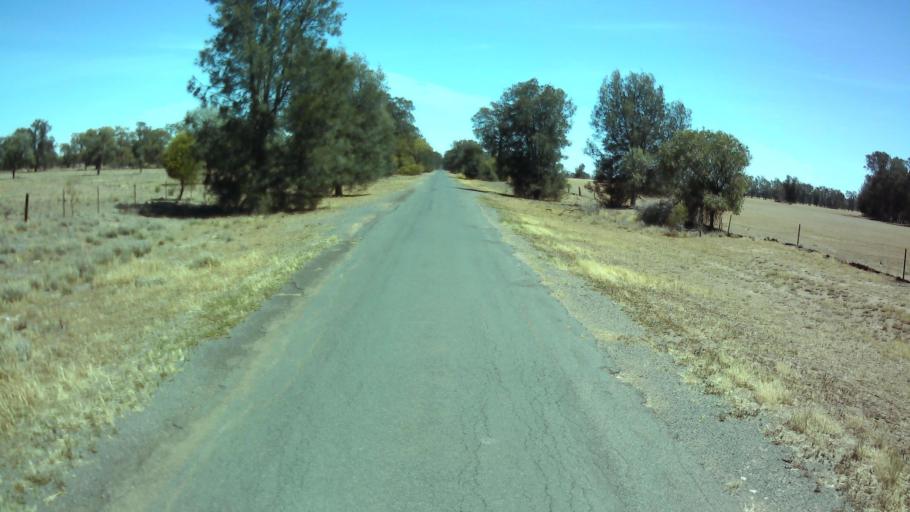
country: AU
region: New South Wales
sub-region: Weddin
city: Grenfell
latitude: -33.8736
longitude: 147.6914
